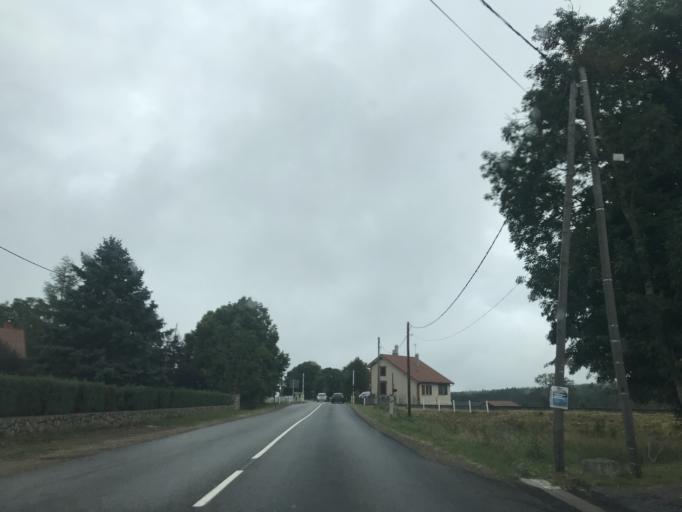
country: FR
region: Auvergne
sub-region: Departement de la Haute-Loire
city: Fontannes
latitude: 45.3252
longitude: 3.6990
